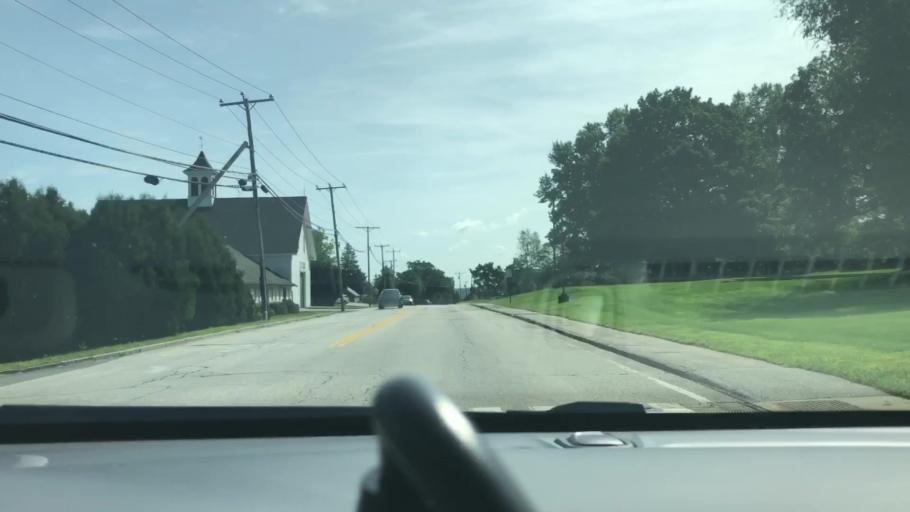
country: US
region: New Hampshire
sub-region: Hillsborough County
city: Pinardville
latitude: 42.9877
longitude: -71.5085
